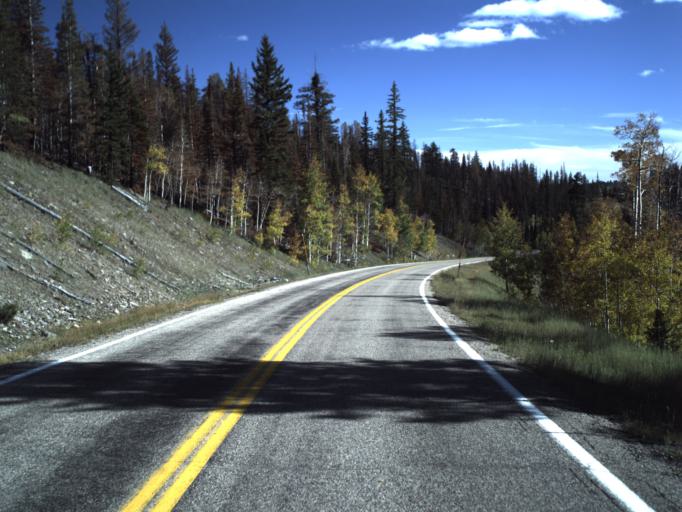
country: US
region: Utah
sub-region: Iron County
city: Parowan
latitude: 37.6627
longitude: -112.7176
